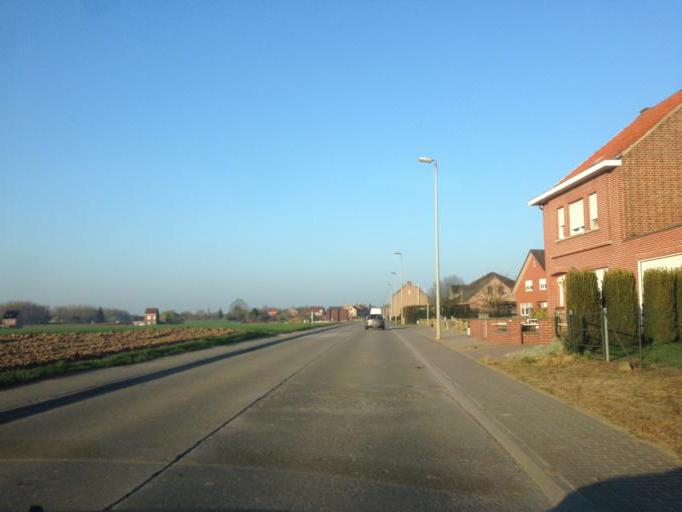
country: BE
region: Flanders
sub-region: Provincie Vlaams-Brabant
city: Boutersem
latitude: 50.8487
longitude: 4.8625
